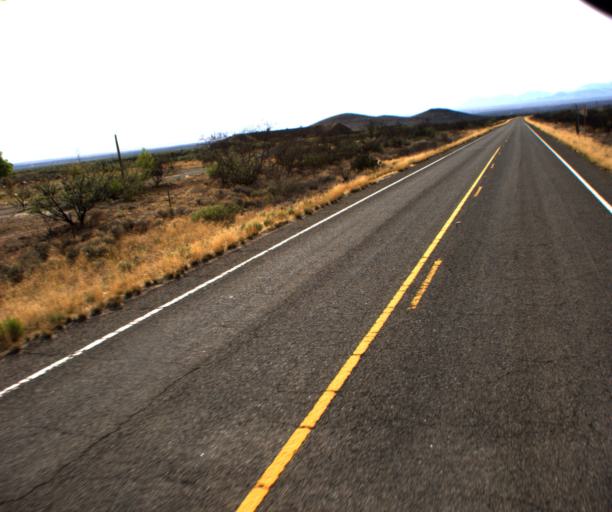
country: US
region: Arizona
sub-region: Cochise County
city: Willcox
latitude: 32.1827
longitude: -109.6643
